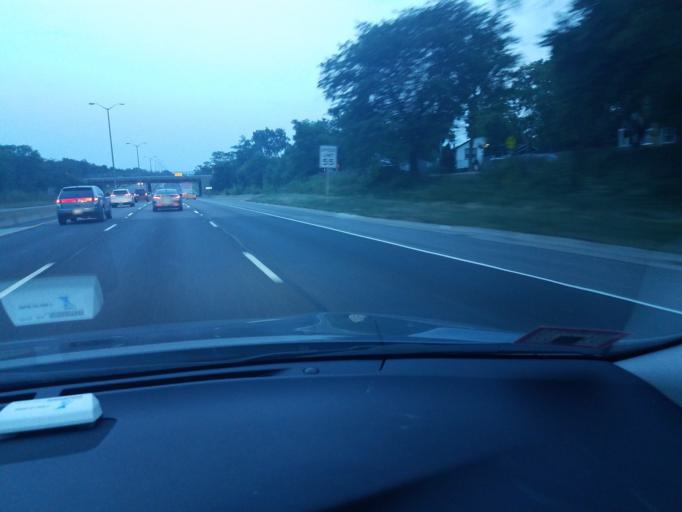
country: US
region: Illinois
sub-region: Cook County
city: Northfield
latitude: 42.0957
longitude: -87.7642
